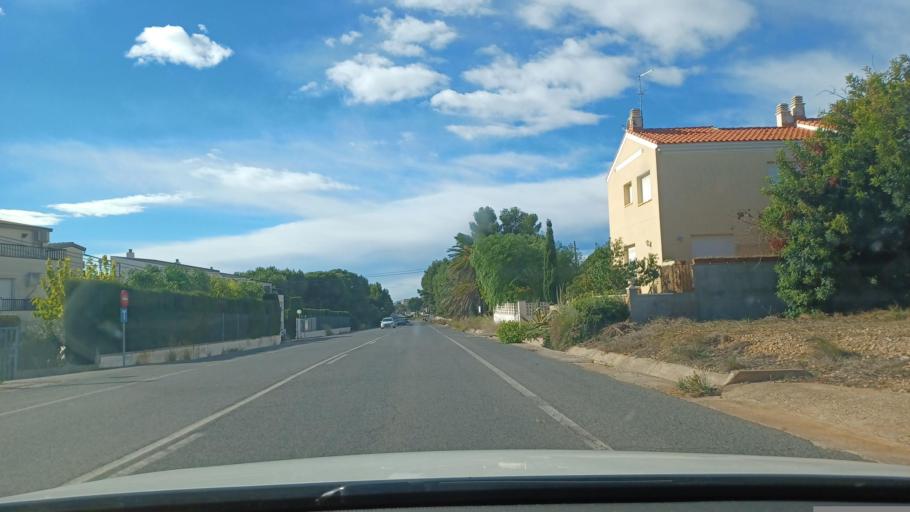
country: ES
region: Catalonia
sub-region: Provincia de Tarragona
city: Sant Carles de la Rapita
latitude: 40.6000
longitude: 0.5753
